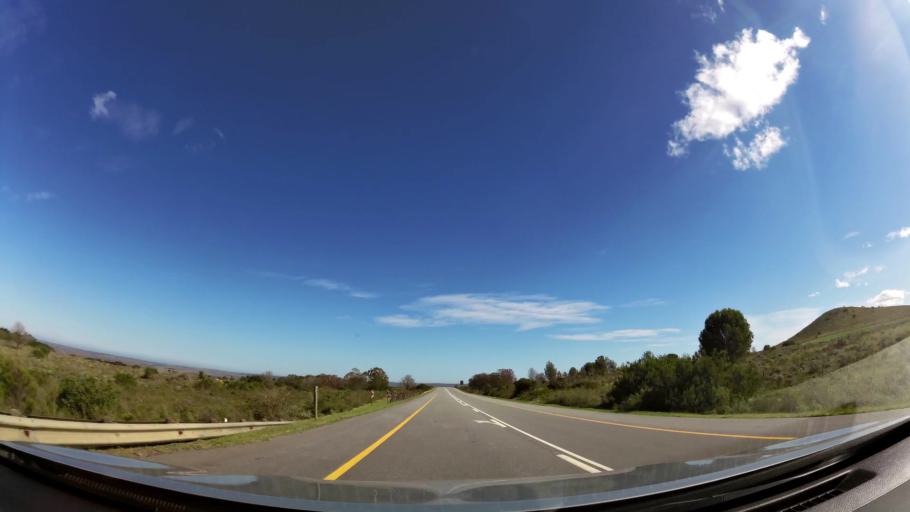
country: ZA
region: Eastern Cape
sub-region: Cacadu District Municipality
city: Kruisfontein
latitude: -33.9966
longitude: 24.6895
